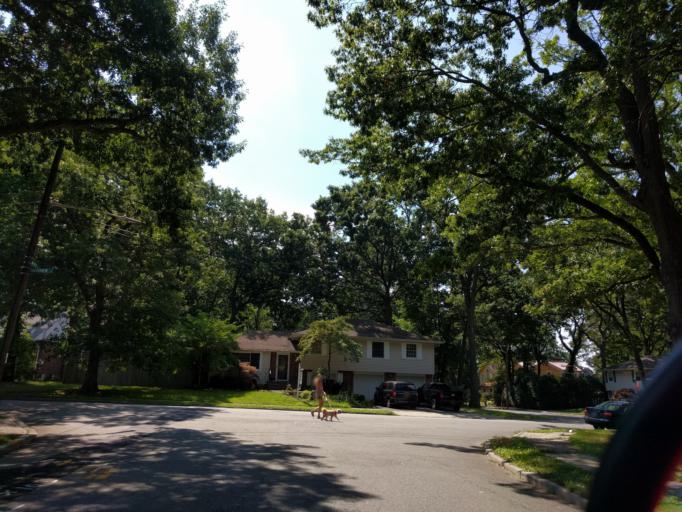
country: US
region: New York
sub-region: Nassau County
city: Oyster Bay
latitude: 40.8583
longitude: -73.5308
